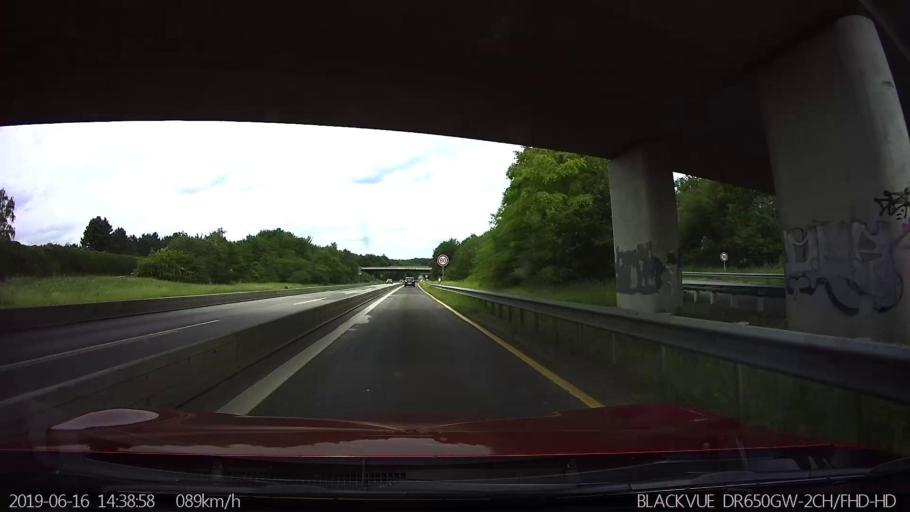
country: DE
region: Schleswig-Holstein
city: Mielkendorf
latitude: 54.3006
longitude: 10.0523
